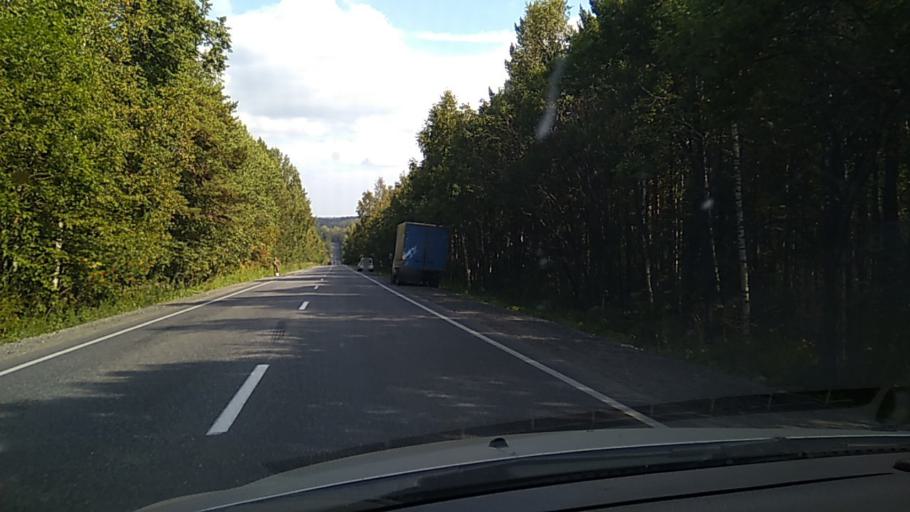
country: RU
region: Chelyabinsk
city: Syrostan
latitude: 55.1197
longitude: 59.8281
